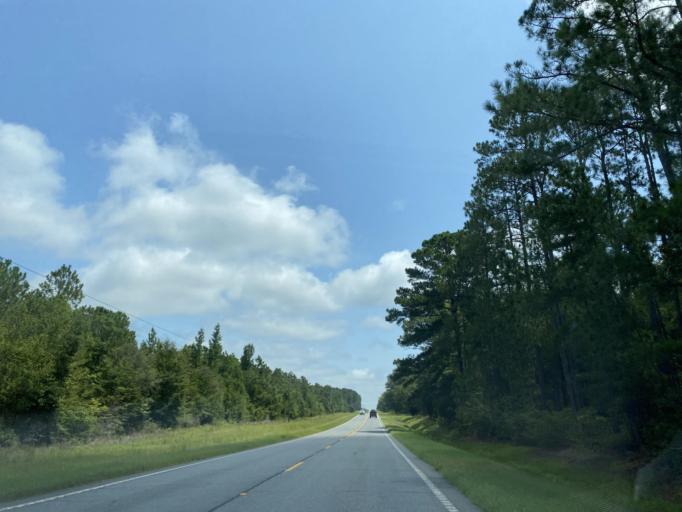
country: US
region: Georgia
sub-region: Telfair County
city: McRae
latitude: 32.1020
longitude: -82.8388
